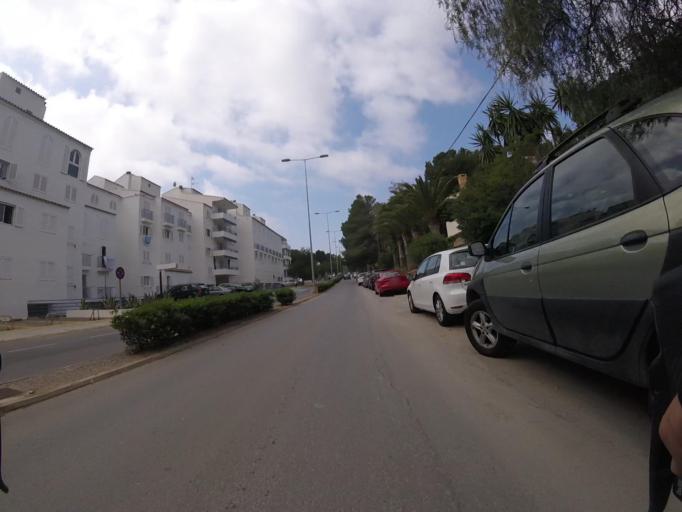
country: ES
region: Valencia
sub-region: Provincia de Castello
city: Alcoceber
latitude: 40.2559
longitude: 0.2872
